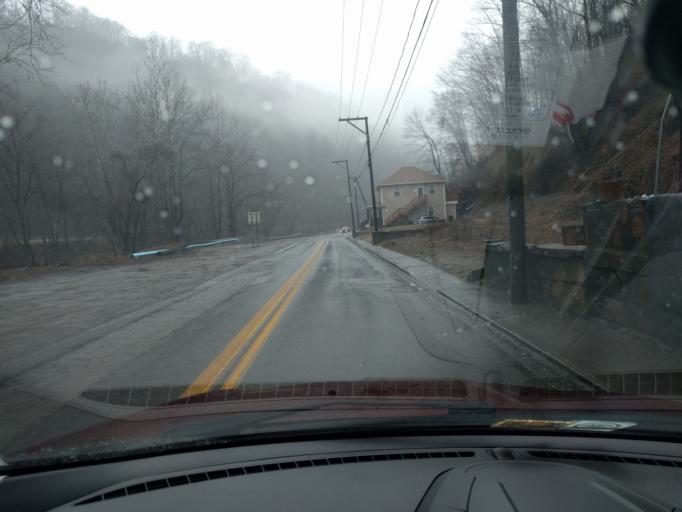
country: US
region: West Virginia
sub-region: McDowell County
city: Welch
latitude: 37.4362
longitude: -81.5877
